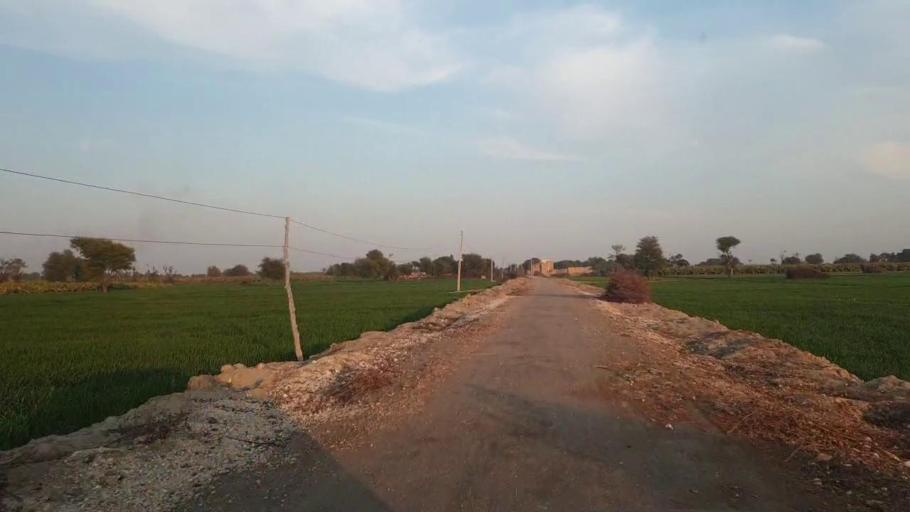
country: PK
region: Sindh
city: Shahpur Chakar
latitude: 26.1947
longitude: 68.6192
